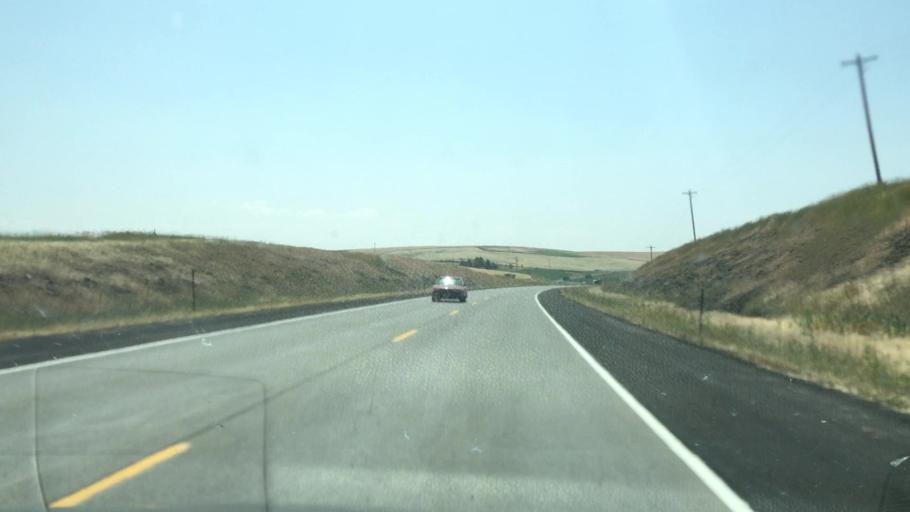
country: US
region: Idaho
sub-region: Lewis County
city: Nezperce
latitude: 46.0746
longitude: -116.3423
